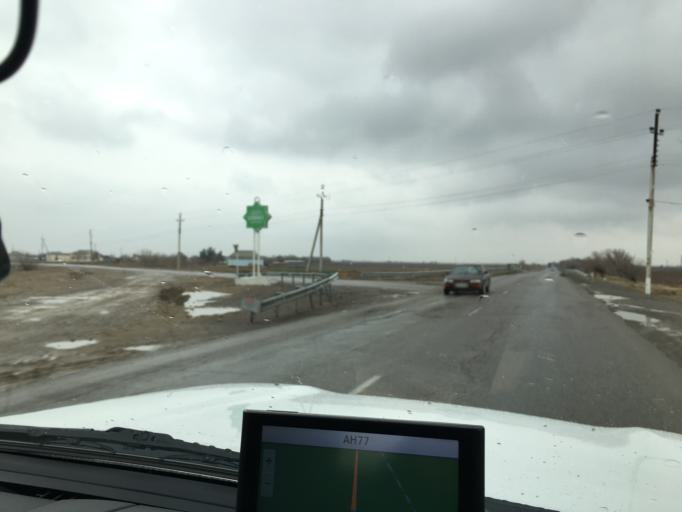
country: TM
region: Mary
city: Yoloeten
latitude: 37.3522
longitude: 62.2518
